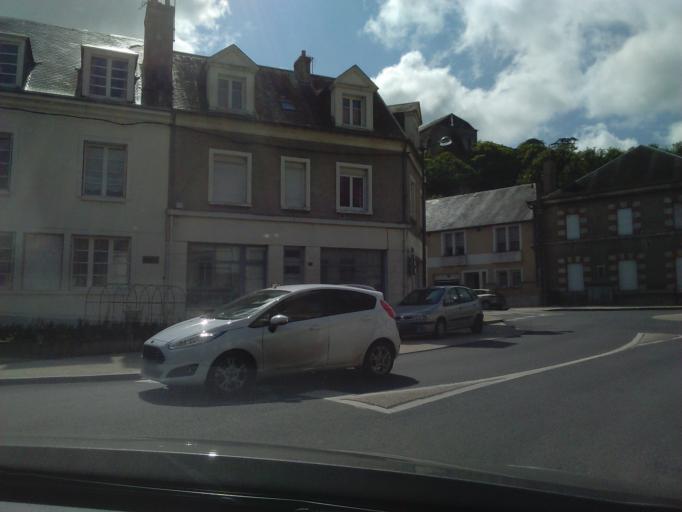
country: FR
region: Centre
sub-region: Departement du Loir-et-Cher
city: Vendome
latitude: 47.7904
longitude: 1.0637
